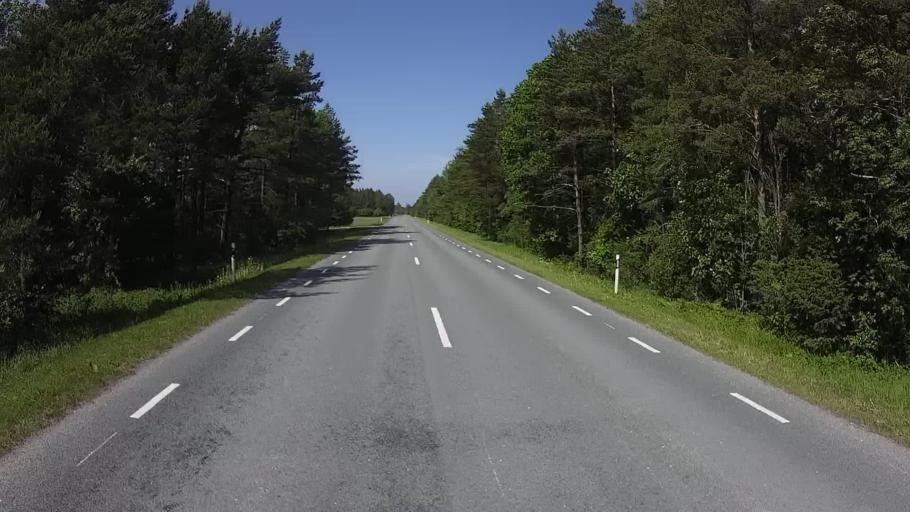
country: EE
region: Saare
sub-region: Kuressaare linn
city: Kuressaare
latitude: 58.3667
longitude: 22.4378
